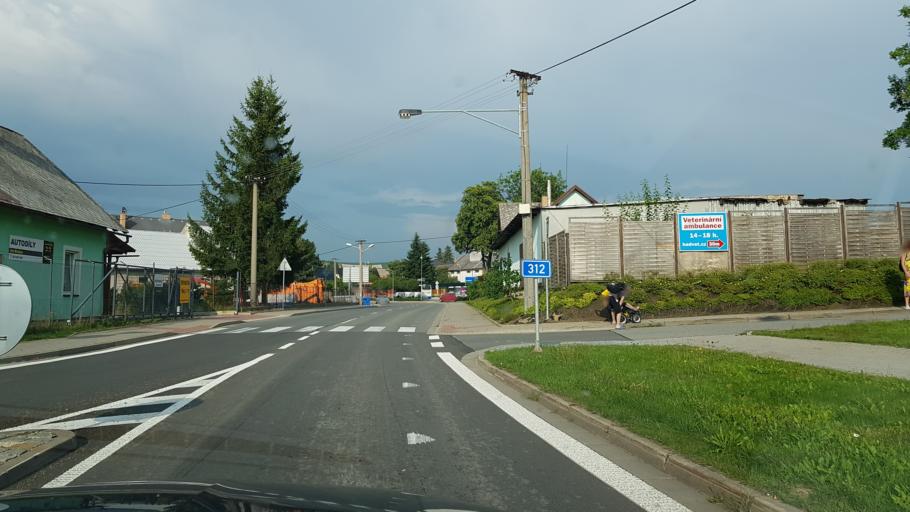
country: CZ
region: Pardubicky
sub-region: Okres Usti nad Orlici
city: Kraliky
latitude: 50.0811
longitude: 16.7616
